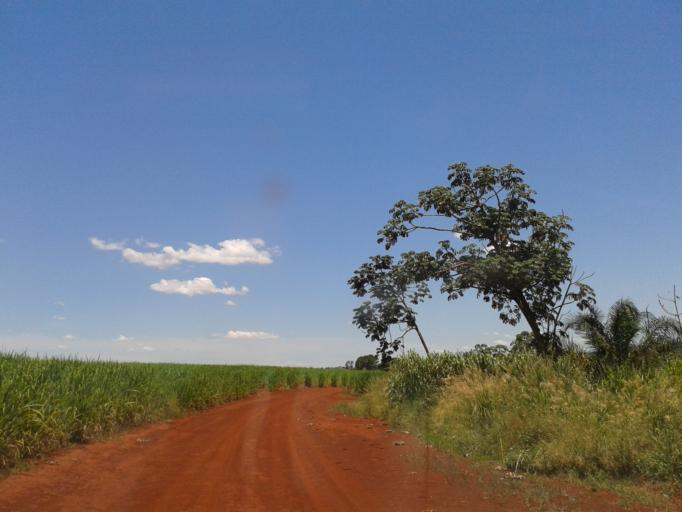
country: BR
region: Minas Gerais
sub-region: Centralina
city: Centralina
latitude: -18.6683
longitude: -49.2409
